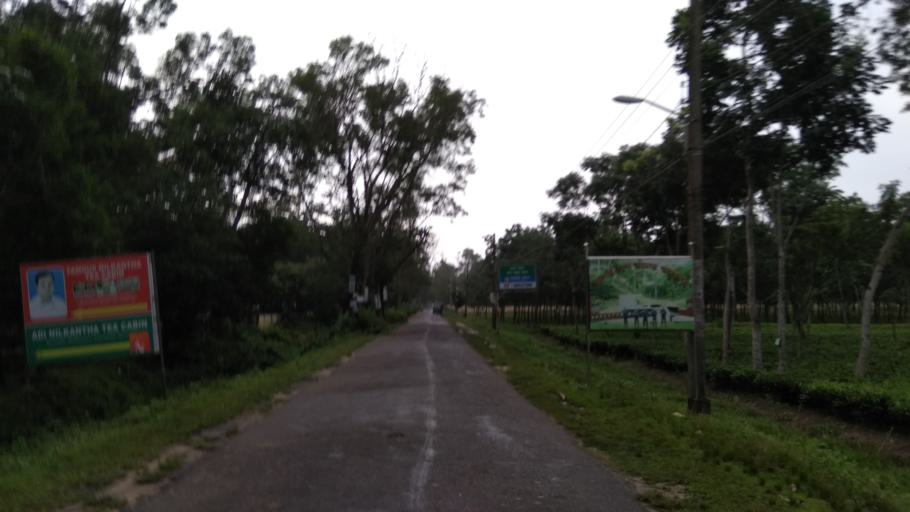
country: IN
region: Tripura
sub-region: Dhalai
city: Kamalpur
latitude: 24.3015
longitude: 91.7350
